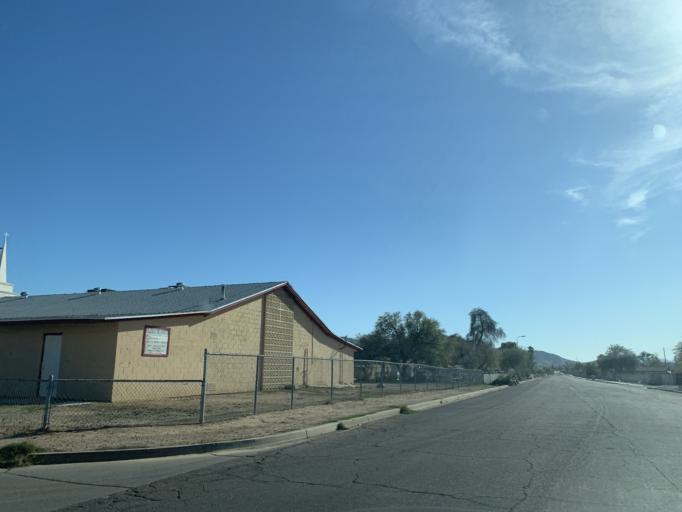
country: US
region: Arizona
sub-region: Maricopa County
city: Laveen
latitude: 33.3960
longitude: -112.1423
